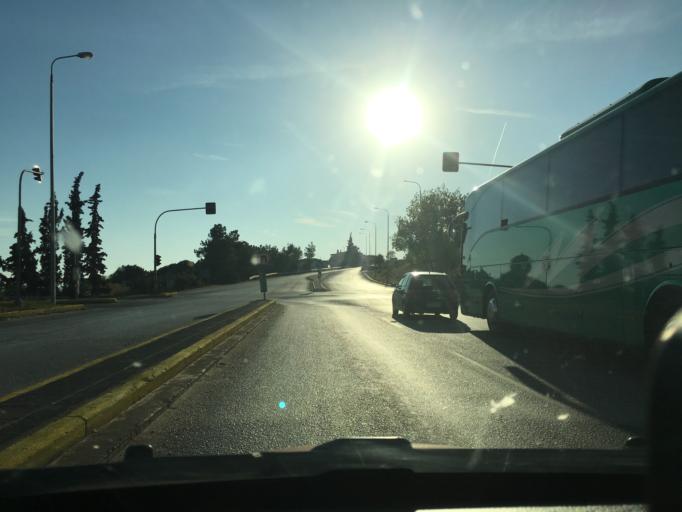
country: GR
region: Central Macedonia
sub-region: Nomos Chalkidikis
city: Nea Moudhania
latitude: 40.2420
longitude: 23.2981
